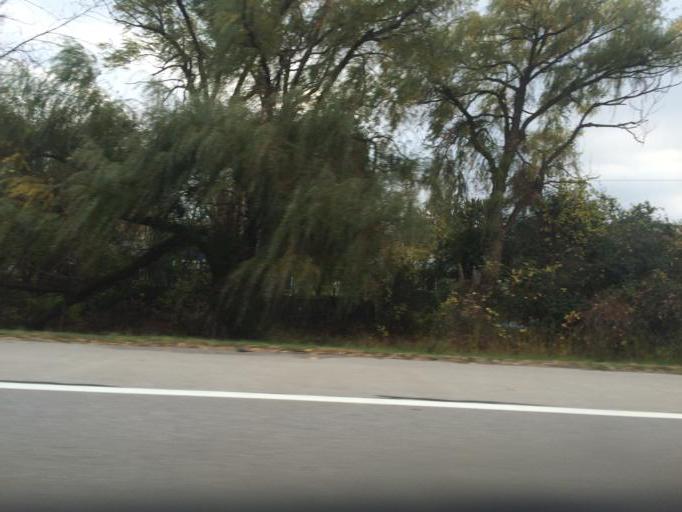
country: US
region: New York
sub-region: Monroe County
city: North Gates
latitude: 43.1569
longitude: -77.6983
